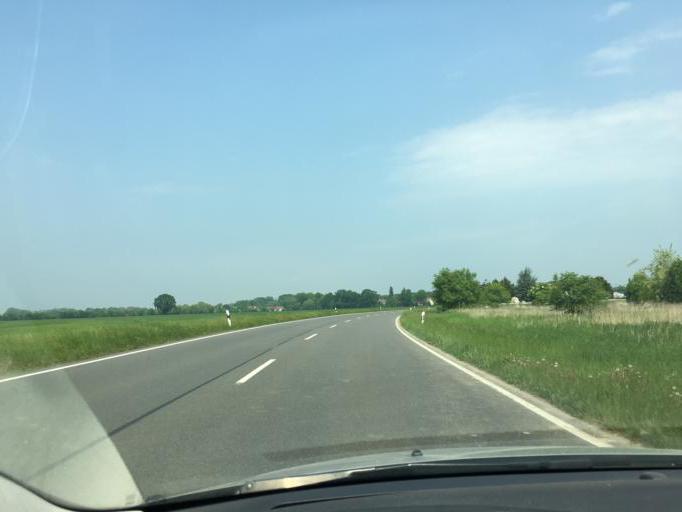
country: DE
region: Saxony
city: Naunhof
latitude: 51.2797
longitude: 12.5753
